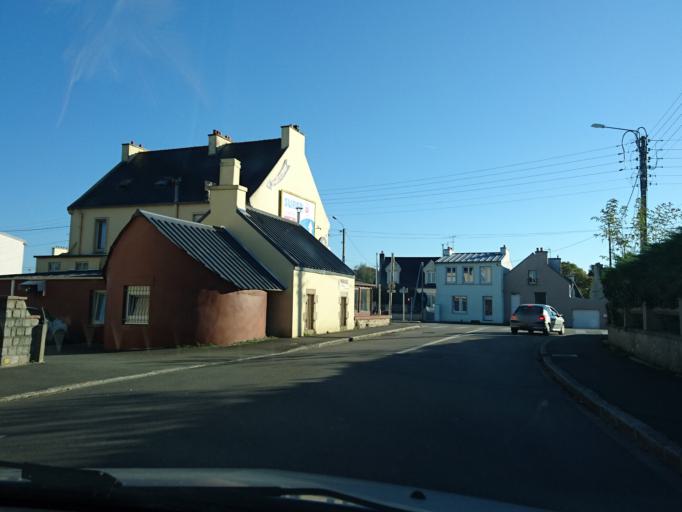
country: FR
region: Brittany
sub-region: Departement du Finistere
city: Brest
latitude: 48.4136
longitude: -4.4509
